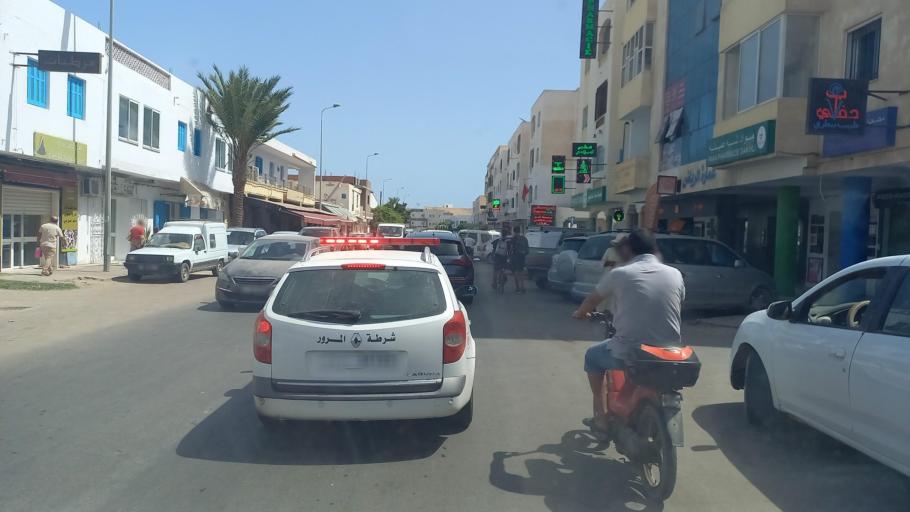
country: TN
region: Madanin
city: Zarzis
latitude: 33.5013
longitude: 11.1041
